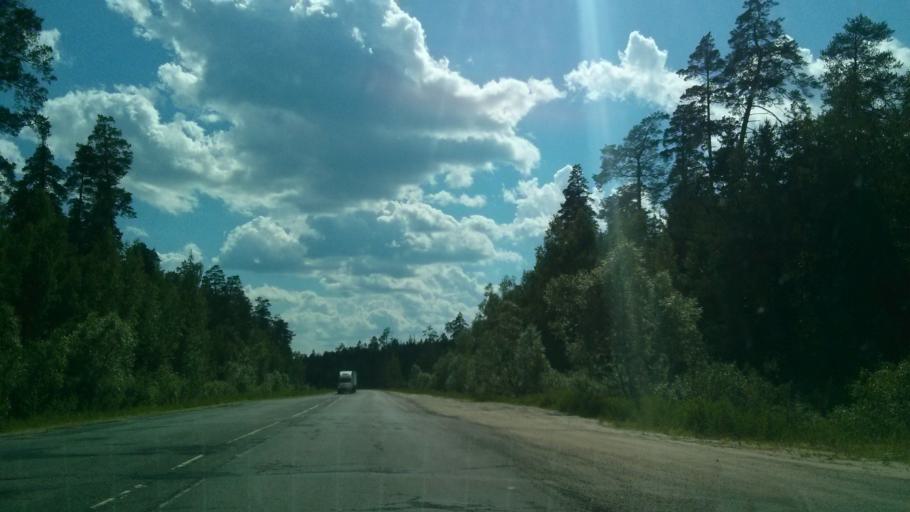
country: RU
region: Vladimir
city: Melenki
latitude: 55.3535
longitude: 41.6800
